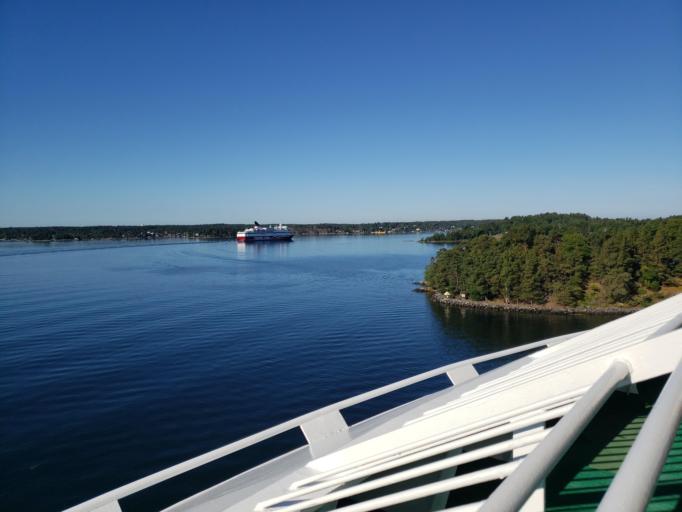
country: SE
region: Stockholm
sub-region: Varmdo Kommun
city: Mortnas
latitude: 59.3644
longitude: 18.4464
